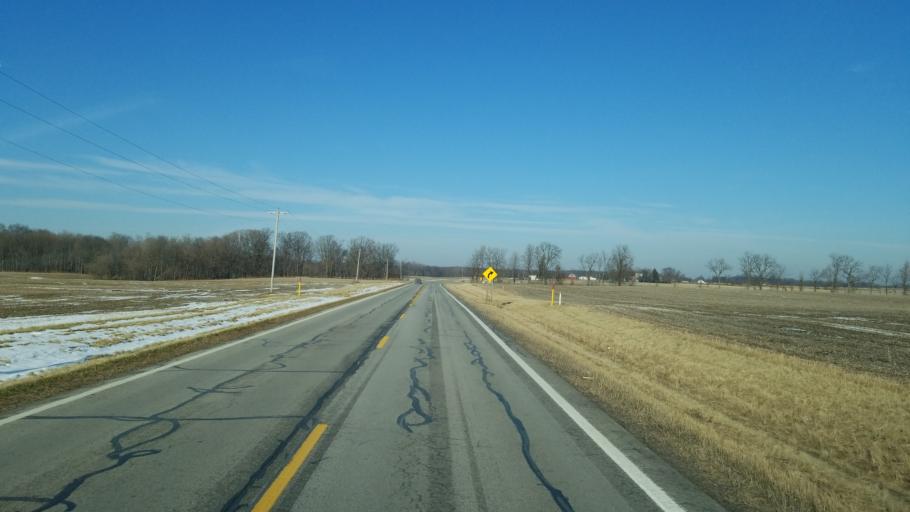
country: US
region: Ohio
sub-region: Huron County
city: Willard
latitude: 41.1229
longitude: -82.6615
